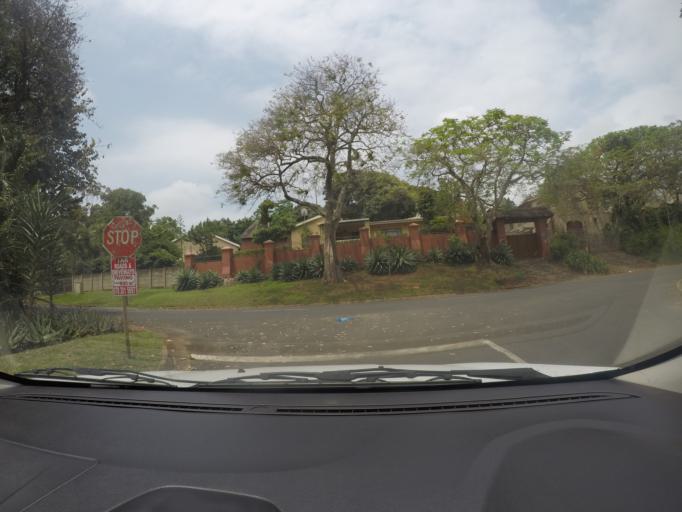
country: ZA
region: KwaZulu-Natal
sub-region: uThungulu District Municipality
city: Empangeni
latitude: -28.7524
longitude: 31.8921
